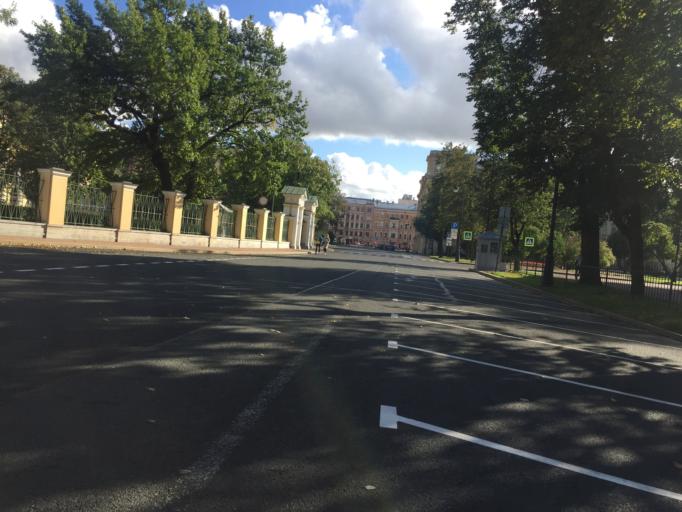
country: RU
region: Leningrad
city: Finlyandskiy
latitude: 59.9468
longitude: 30.3952
